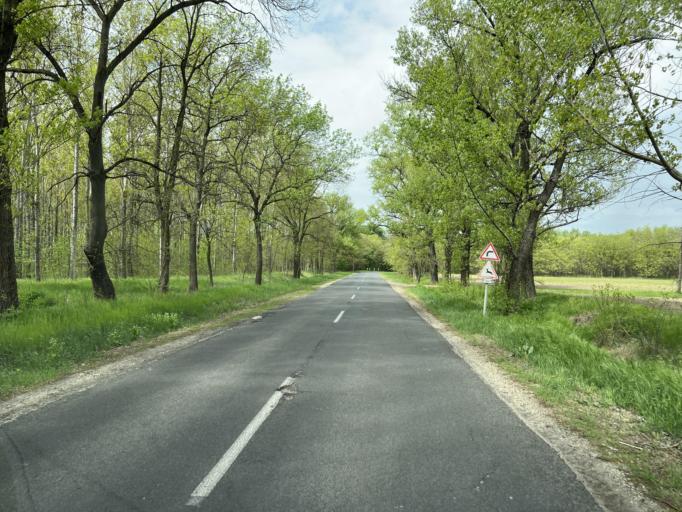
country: HU
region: Pest
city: Tortel
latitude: 47.1451
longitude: 19.8719
